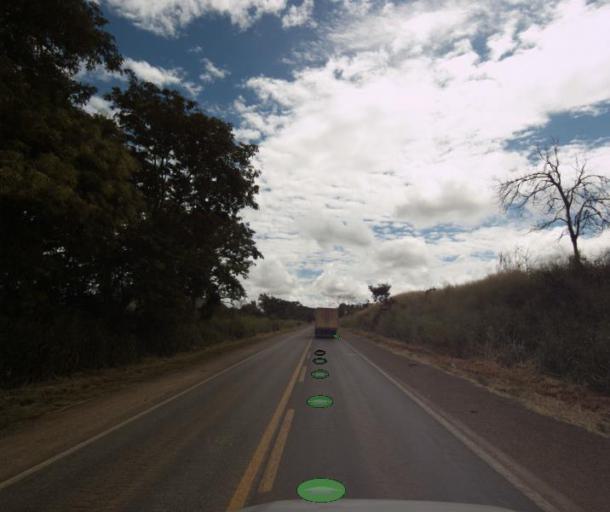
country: BR
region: Goias
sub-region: Uruacu
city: Uruacu
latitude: -14.4090
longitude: -49.1574
